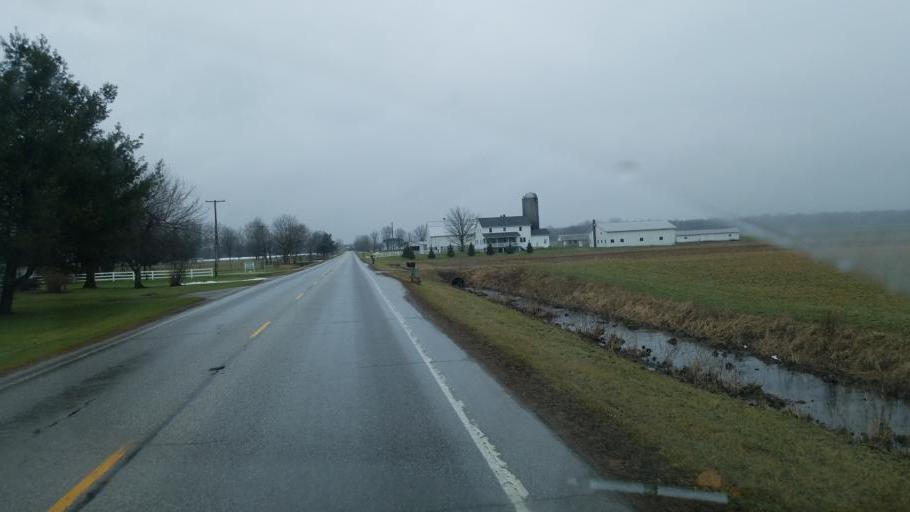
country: US
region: Ohio
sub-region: Geauga County
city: Middlefield
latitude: 41.4153
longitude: -80.9550
